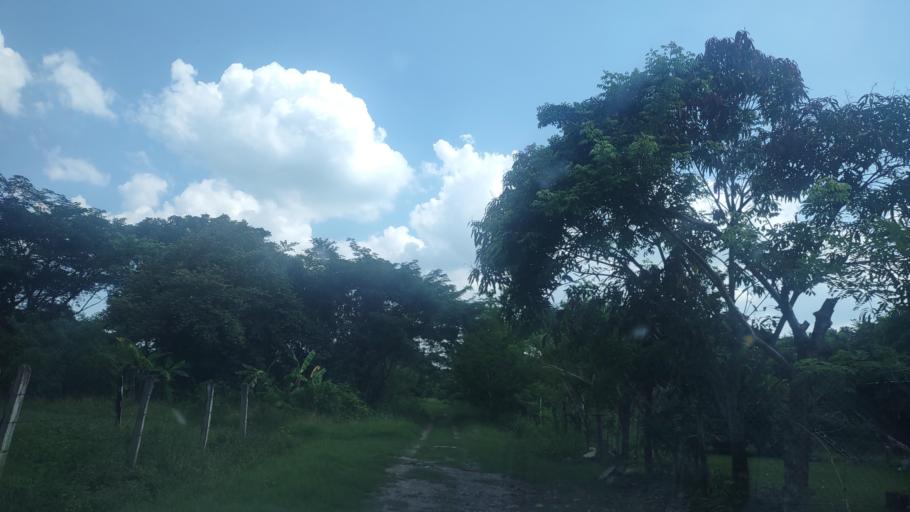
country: MX
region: Veracruz
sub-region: Chinampa de Gorostiza
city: Colonia las Flores
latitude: 21.3688
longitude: -97.6841
